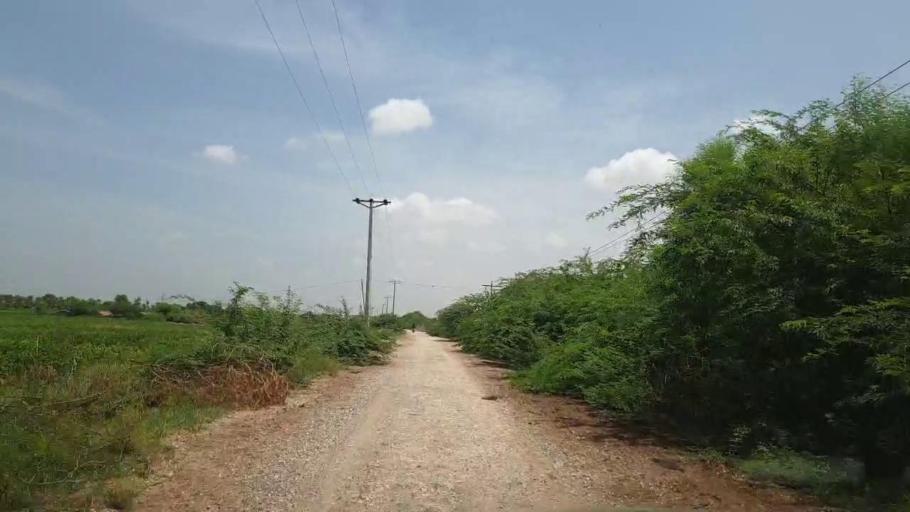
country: PK
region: Sindh
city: Kot Diji
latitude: 27.1400
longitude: 69.0114
